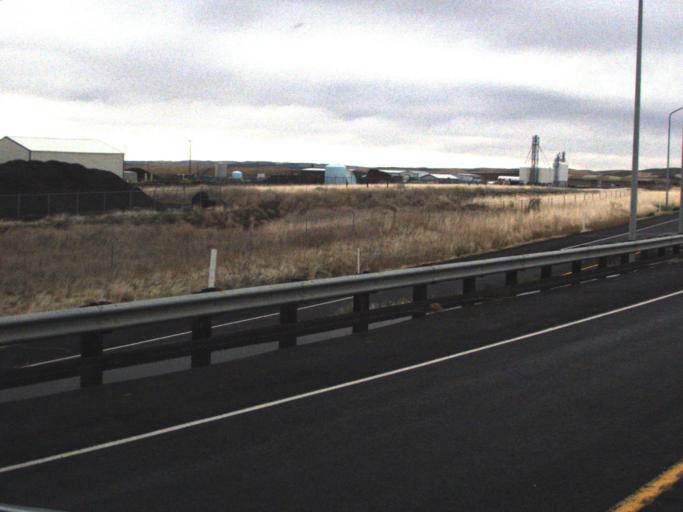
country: US
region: Washington
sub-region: Walla Walla County
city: Walla Walla East
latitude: 46.0894
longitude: -118.2583
